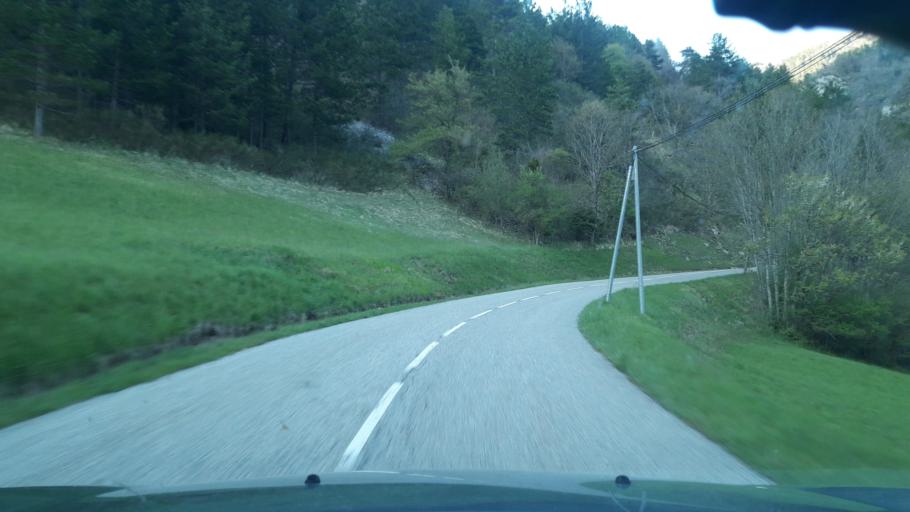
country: FR
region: Rhone-Alpes
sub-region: Departement de l'Isere
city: Mens
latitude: 44.6960
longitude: 5.6130
